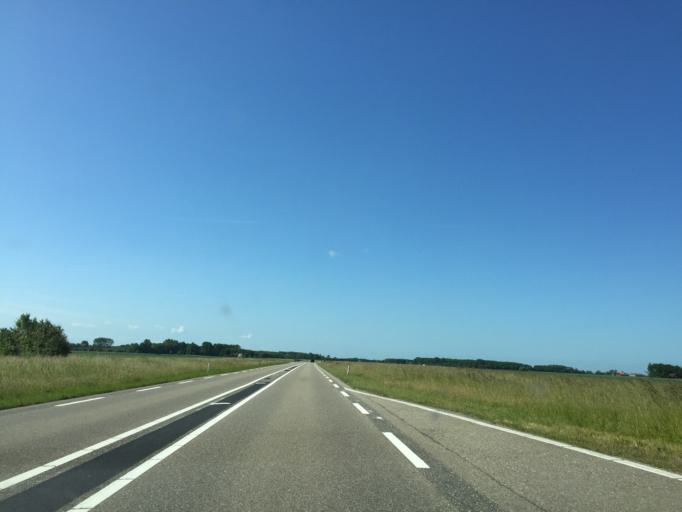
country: NL
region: Zeeland
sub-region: Schouwen-Duiveland
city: Scharendijke
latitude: 51.7156
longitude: 3.8161
